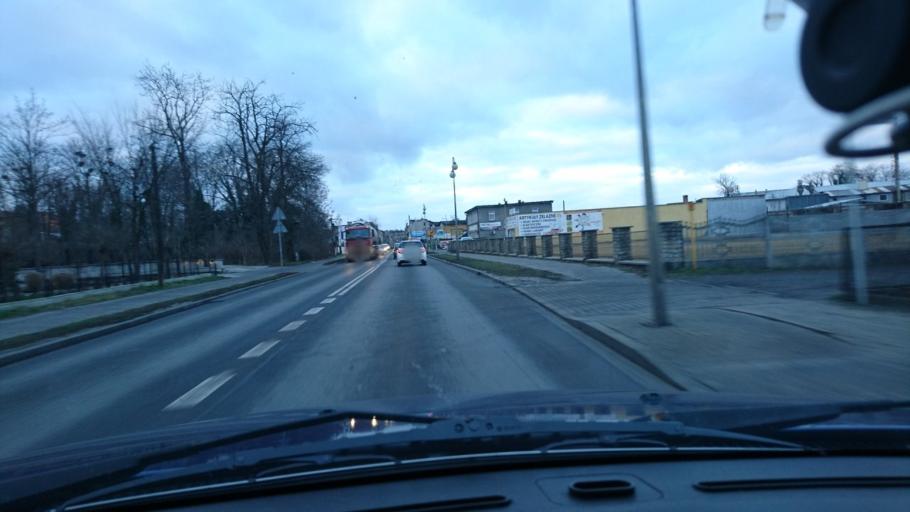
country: PL
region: Greater Poland Voivodeship
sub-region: Powiat kepinski
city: Kepno
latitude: 51.2742
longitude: 17.9904
